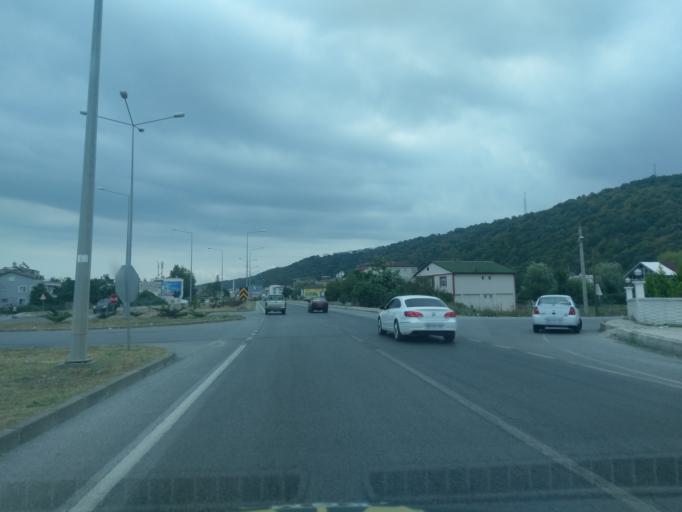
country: TR
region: Samsun
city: Taflan
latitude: 41.3916
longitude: 36.2016
